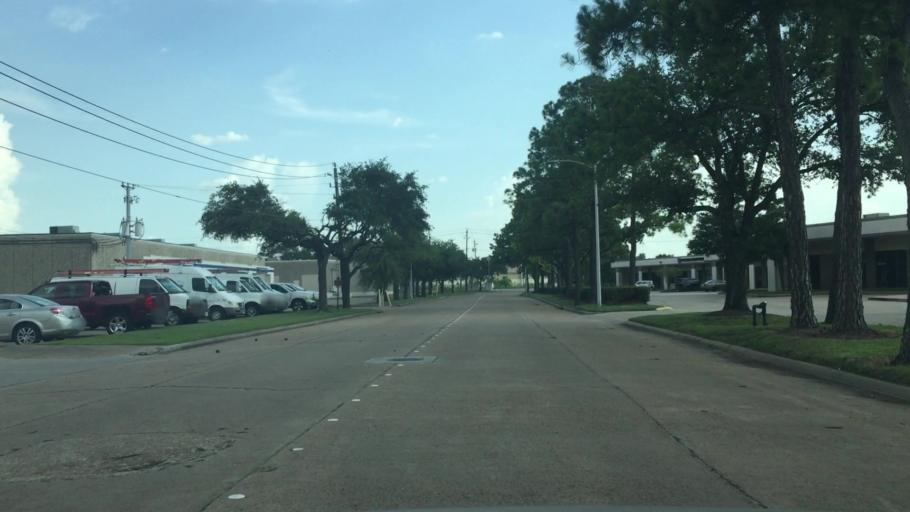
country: US
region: Texas
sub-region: Harris County
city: Spring Valley
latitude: 29.8099
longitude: -95.4684
